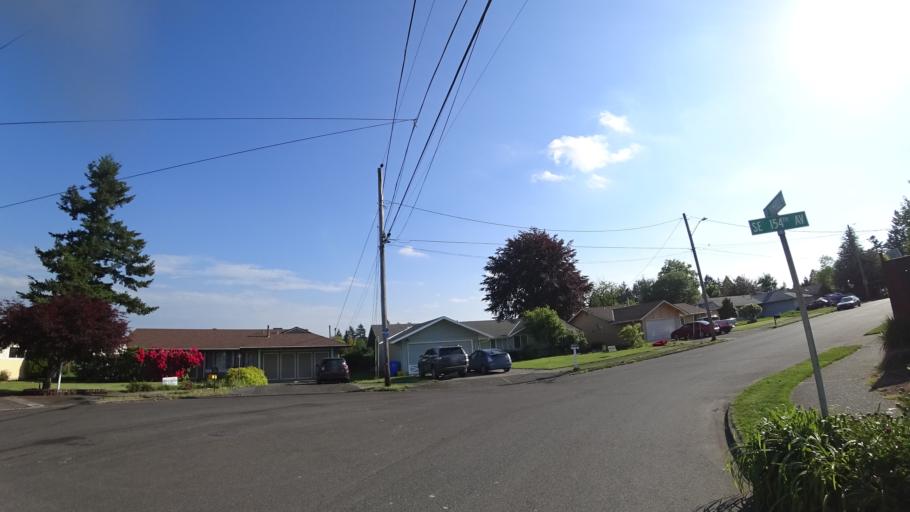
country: US
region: Oregon
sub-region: Multnomah County
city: Lents
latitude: 45.5161
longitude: -122.5053
